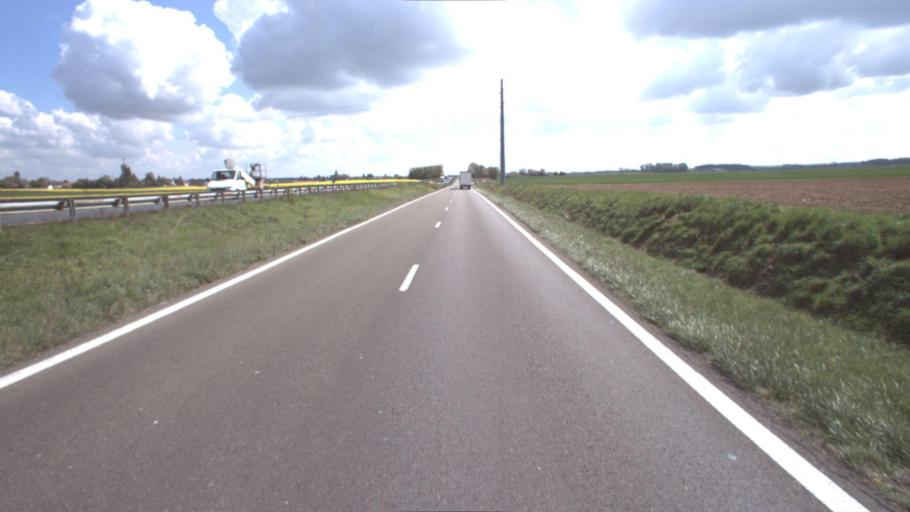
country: FR
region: Ile-de-France
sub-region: Departement de Seine-et-Marne
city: Jouy-le-Chatel
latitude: 48.6847
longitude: 3.0655
